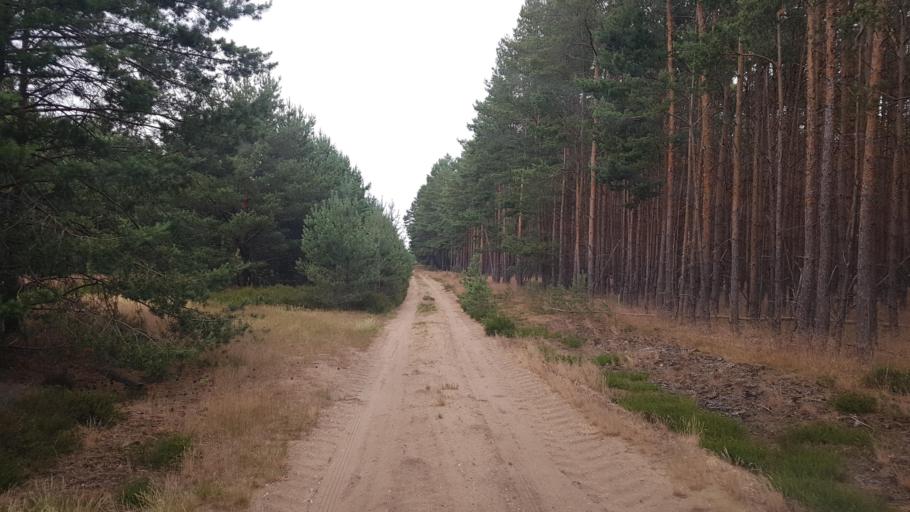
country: DE
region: Brandenburg
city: Treuenbrietzen
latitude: 52.0572
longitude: 12.8119
